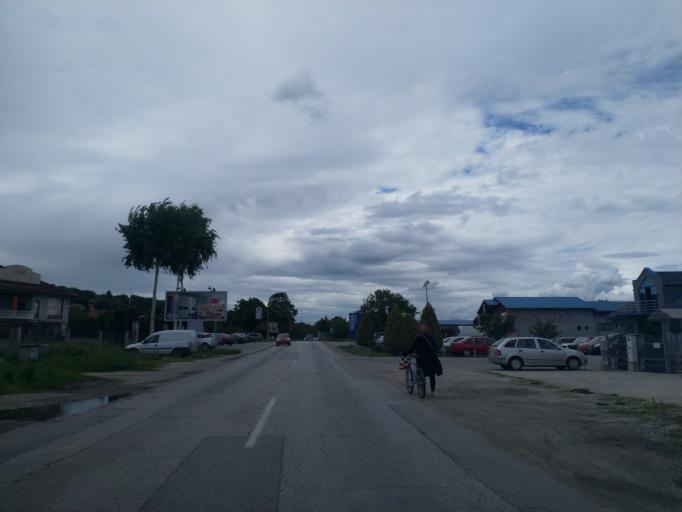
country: RS
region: Central Serbia
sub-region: Pomoravski Okrug
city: Jagodina
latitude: 43.9611
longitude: 21.2828
